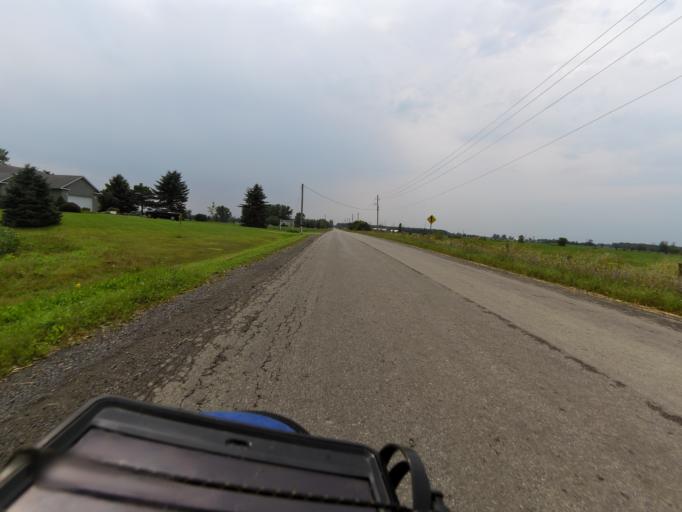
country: CA
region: Ontario
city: Casselman
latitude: 45.1724
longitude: -75.3765
